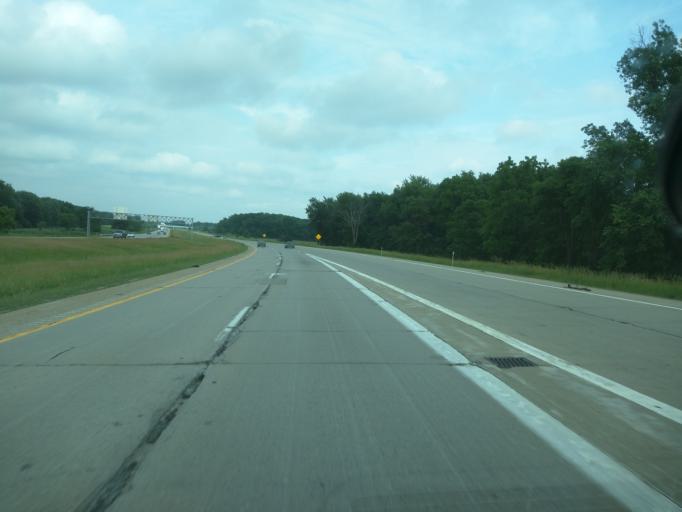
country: US
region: Michigan
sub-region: Clinton County
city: Bath
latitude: 42.8024
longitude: -84.5010
